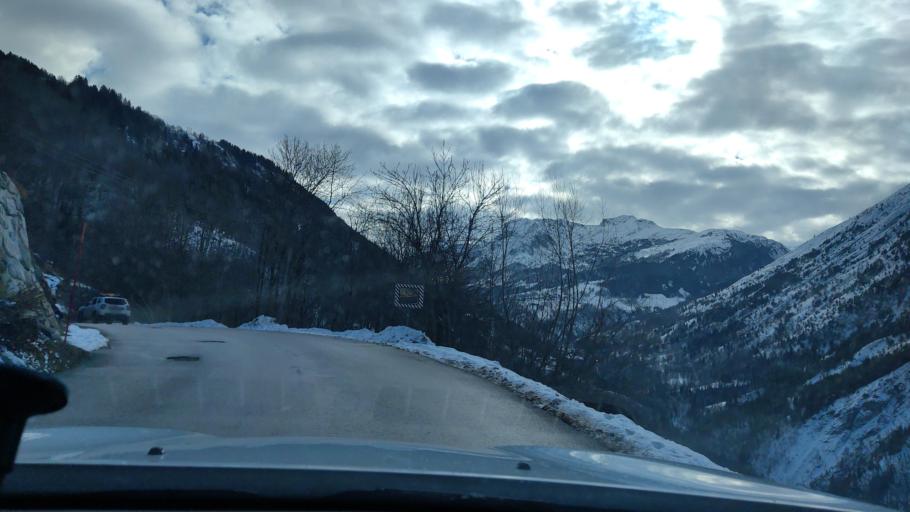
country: FR
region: Rhone-Alpes
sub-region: Departement de la Savoie
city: Saint-Martin-de-Belleville
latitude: 45.4109
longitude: 6.4939
